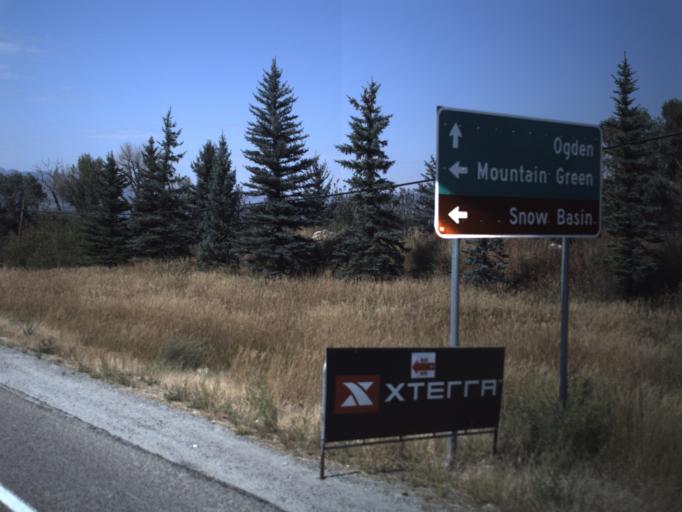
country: US
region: Utah
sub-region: Weber County
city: Wolf Creek
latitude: 41.2473
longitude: -111.7743
